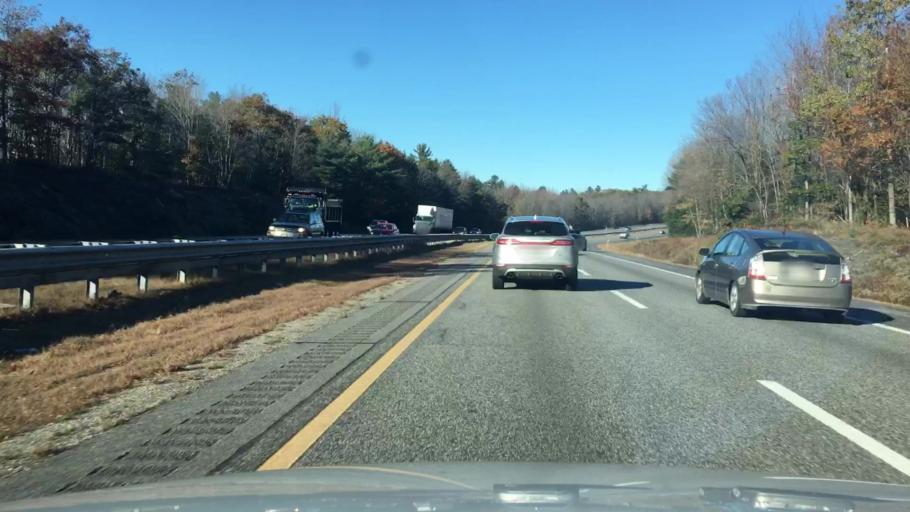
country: US
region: Maine
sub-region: Cumberland County
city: Freeport
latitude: 43.8960
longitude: -70.0778
